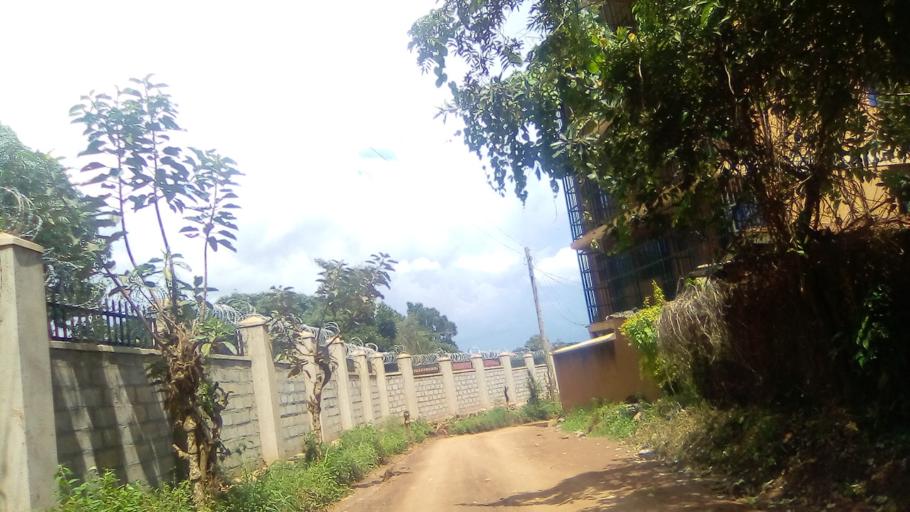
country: UG
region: Central Region
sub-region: Wakiso District
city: Entebbe
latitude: 0.0946
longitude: 32.5080
